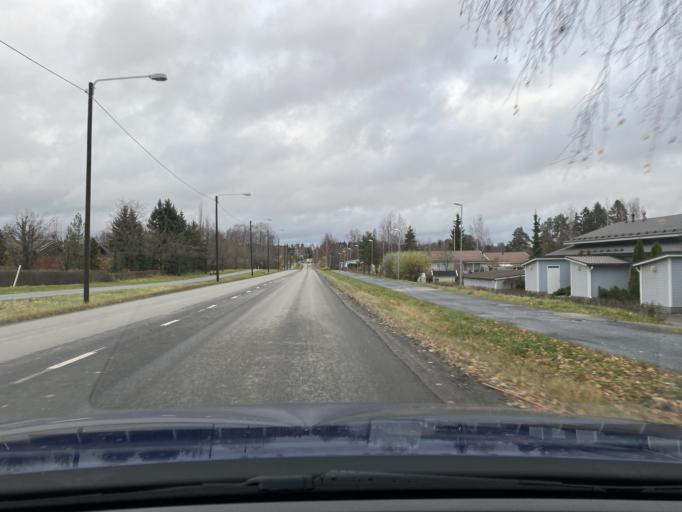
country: FI
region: Pirkanmaa
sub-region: Tampere
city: Lempaeaelae
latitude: 61.3268
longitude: 23.7488
